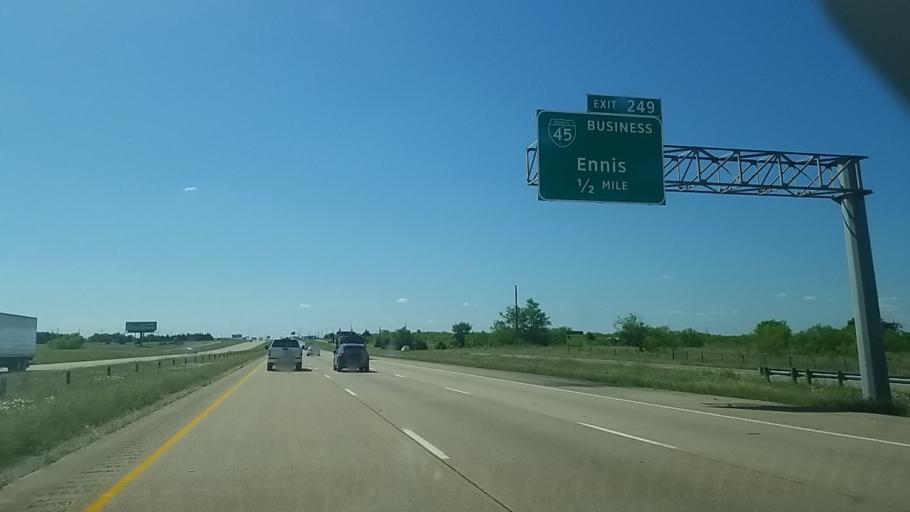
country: US
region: Texas
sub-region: Ellis County
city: Ennis
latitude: 32.3013
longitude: -96.5768
